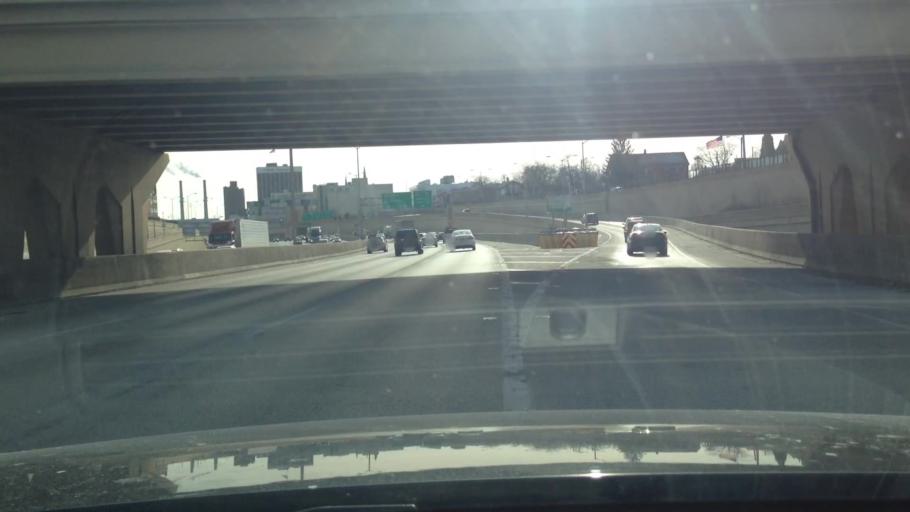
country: US
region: Wisconsin
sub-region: Milwaukee County
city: Milwaukee
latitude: 43.0488
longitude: -87.9264
